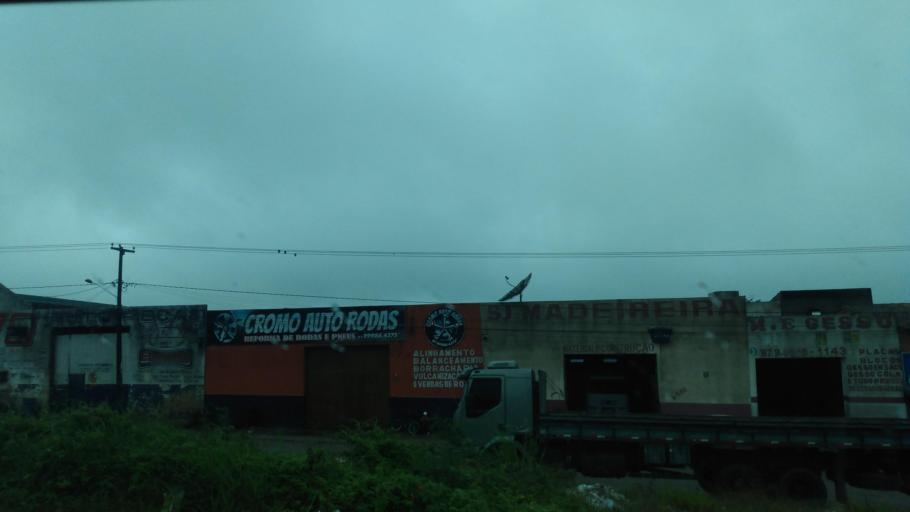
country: BR
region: Pernambuco
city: Garanhuns
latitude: -8.8805
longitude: -36.4930
